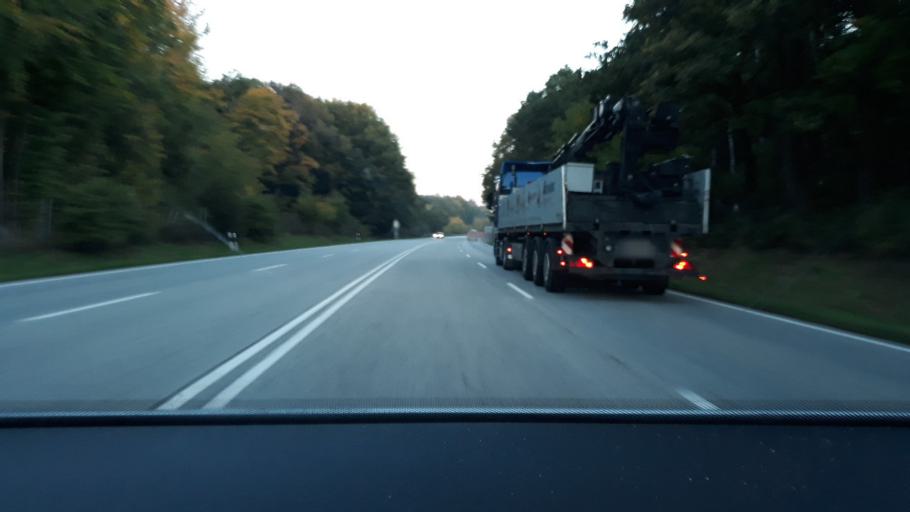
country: DE
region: Schleswig-Holstein
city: Schuby
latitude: 54.5188
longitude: 9.5122
